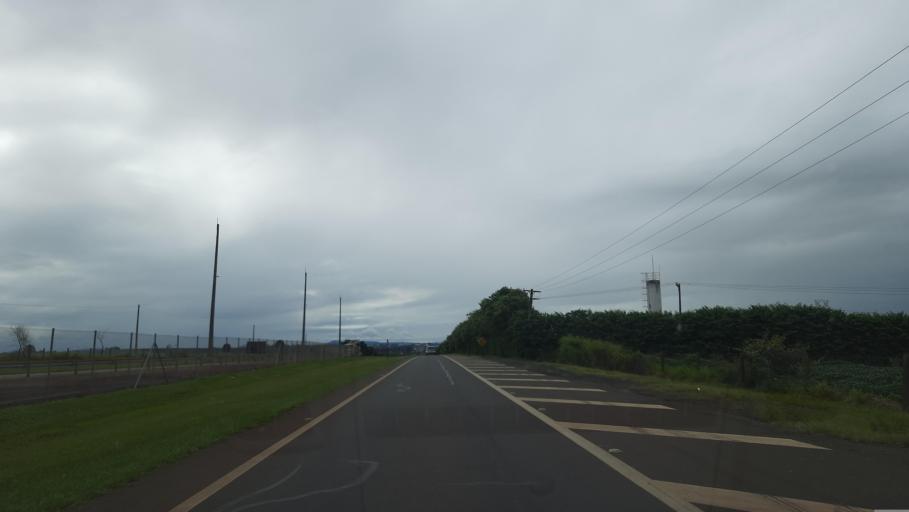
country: BR
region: Sao Paulo
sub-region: Vargem Grande Do Sul
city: Vargem Grande do Sul
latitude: -21.8133
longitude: -46.9852
